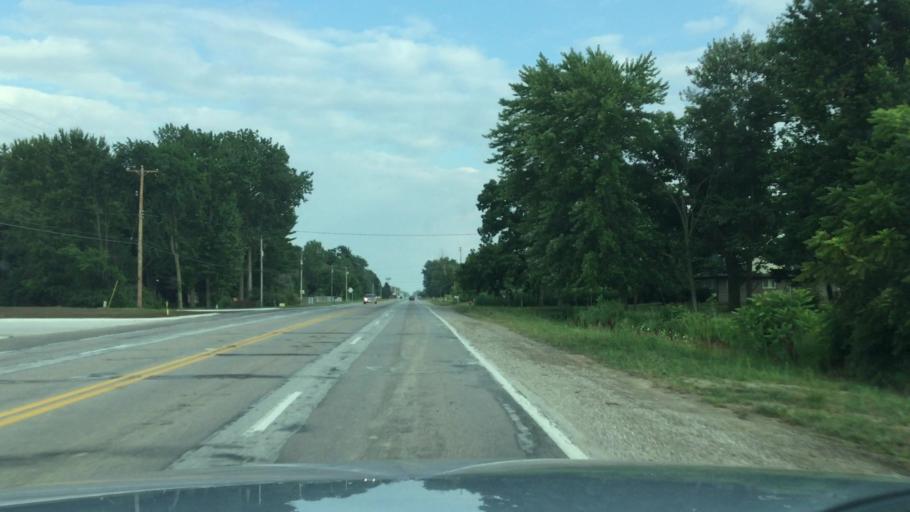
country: US
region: Michigan
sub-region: Saginaw County
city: Birch Run
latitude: 43.2618
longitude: -83.7782
